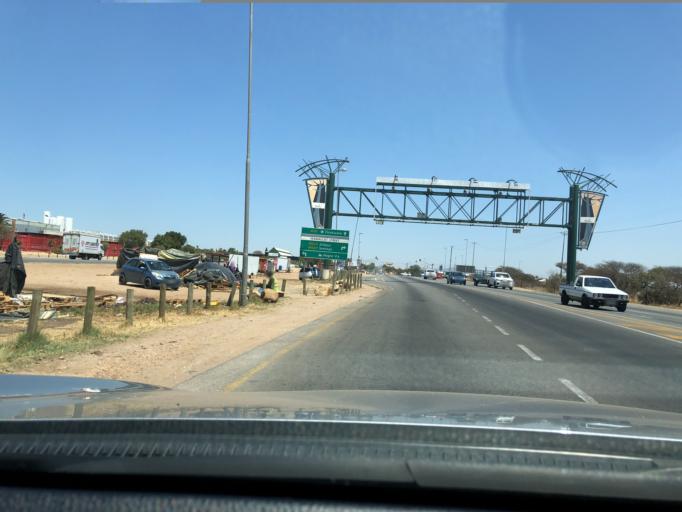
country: ZA
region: Limpopo
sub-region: Capricorn District Municipality
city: Polokwane
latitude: -23.8710
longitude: 29.4652
